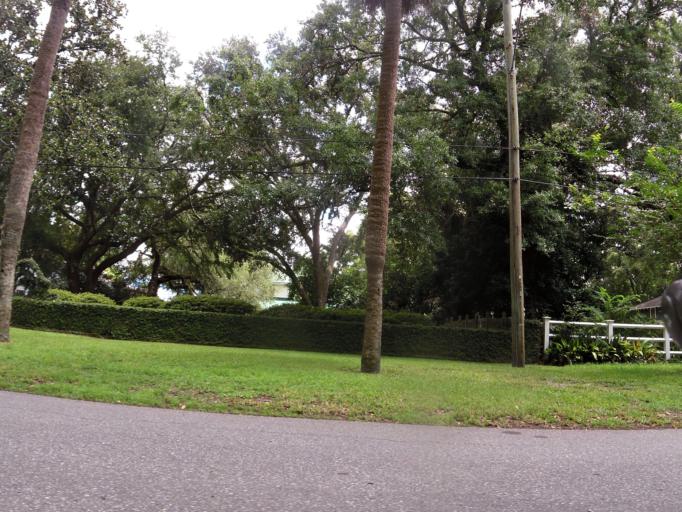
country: US
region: Florida
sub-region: Duval County
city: Jacksonville
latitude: 30.2809
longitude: -81.7122
